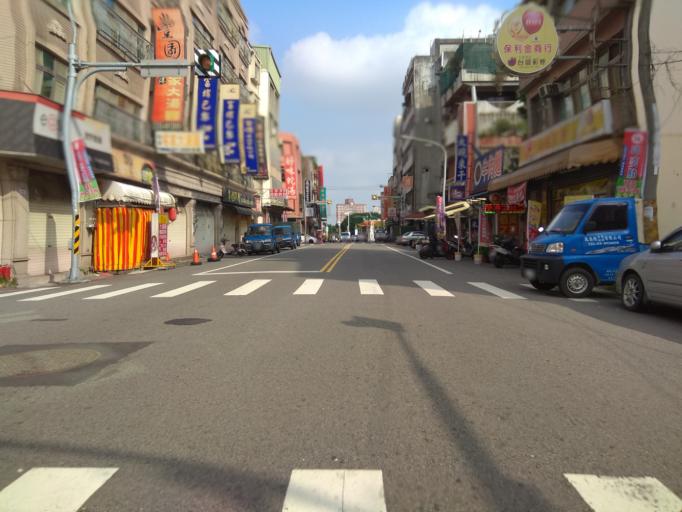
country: TW
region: Taiwan
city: Taoyuan City
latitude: 24.9571
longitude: 121.2181
